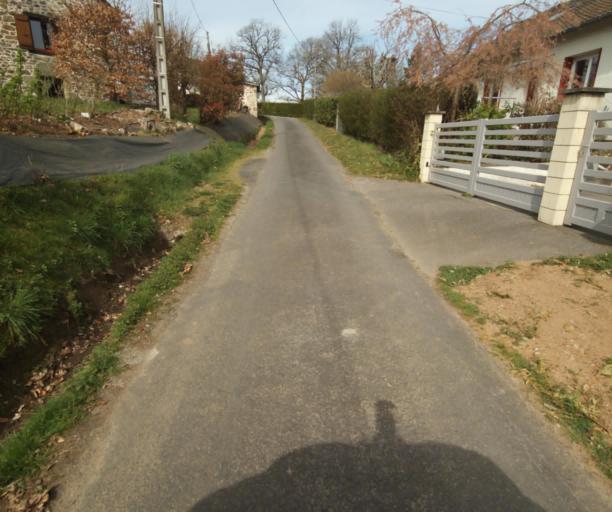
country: FR
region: Limousin
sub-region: Departement de la Correze
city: Correze
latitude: 45.3701
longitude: 1.8206
